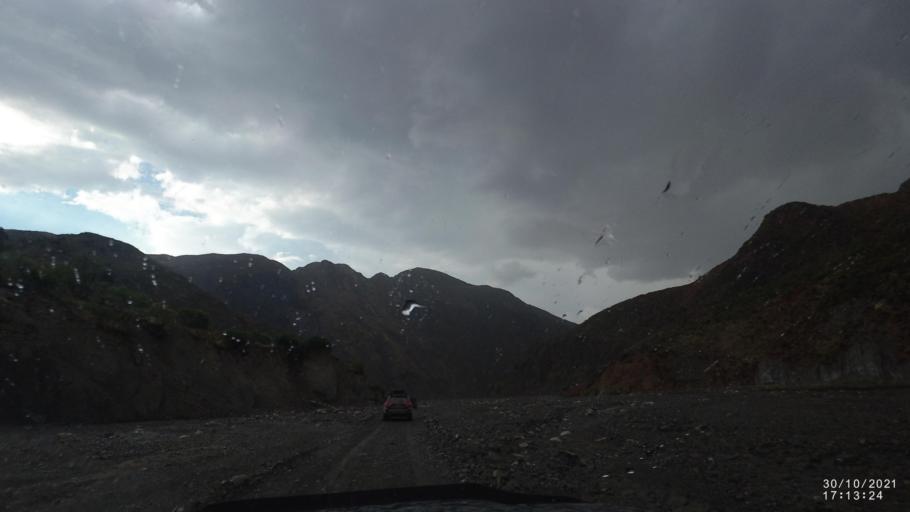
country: BO
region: Cochabamba
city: Colchani
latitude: -17.5489
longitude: -66.6259
